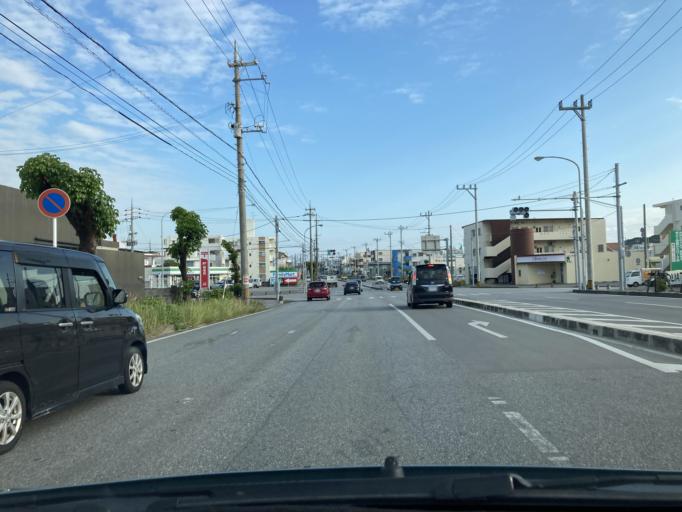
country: JP
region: Okinawa
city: Okinawa
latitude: 26.3508
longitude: 127.8297
